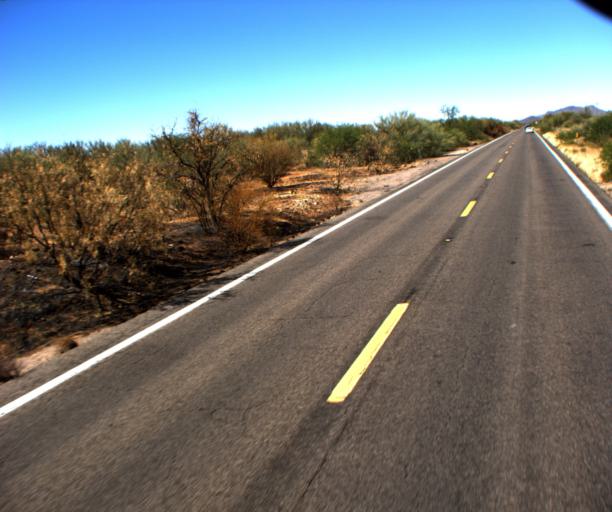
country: US
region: Arizona
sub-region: Pima County
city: Sells
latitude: 31.9686
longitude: -111.7442
